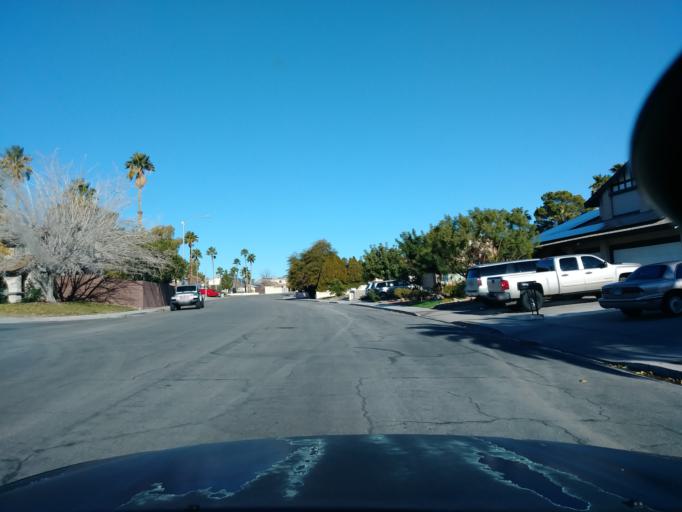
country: US
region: Nevada
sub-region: Clark County
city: Spring Valley
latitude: 36.1485
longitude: -115.2298
